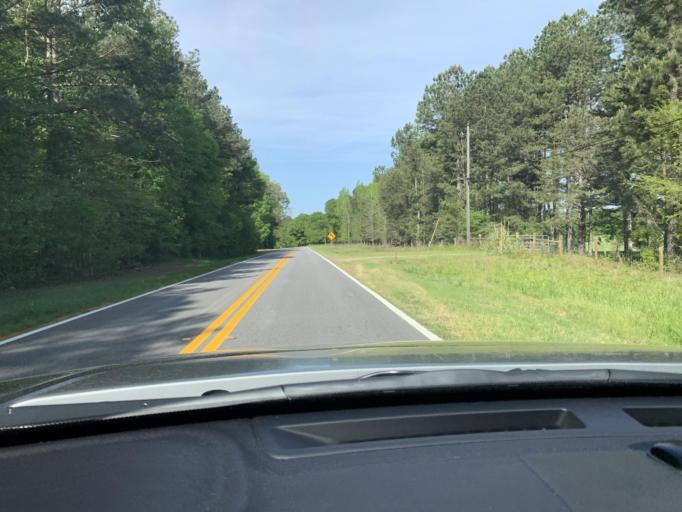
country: US
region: Georgia
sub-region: Oconee County
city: Watkinsville
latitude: 33.8177
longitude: -83.3730
